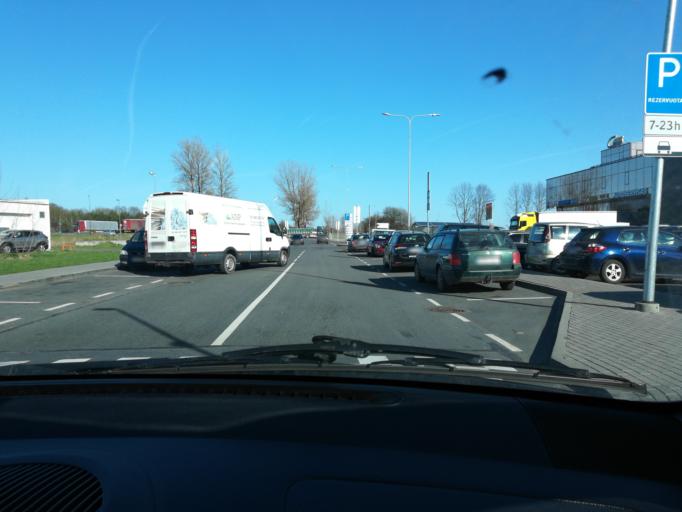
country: LT
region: Vilnius County
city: Rasos
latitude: 54.6525
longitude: 25.3051
